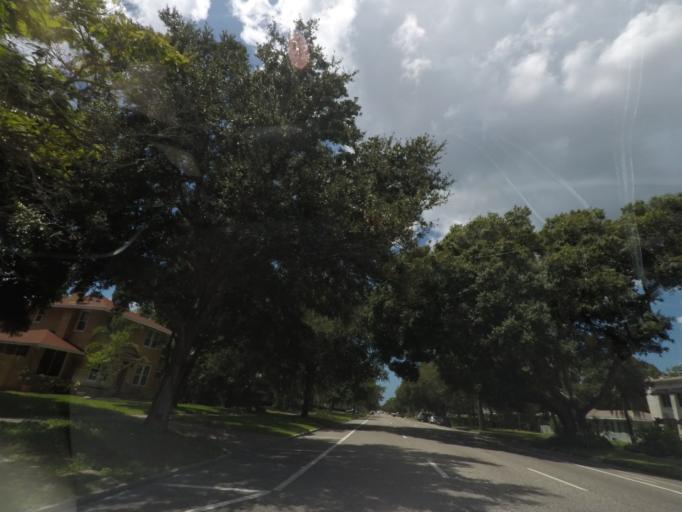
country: US
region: Florida
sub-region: Pinellas County
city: Gulfport
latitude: 27.7718
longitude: -82.7067
